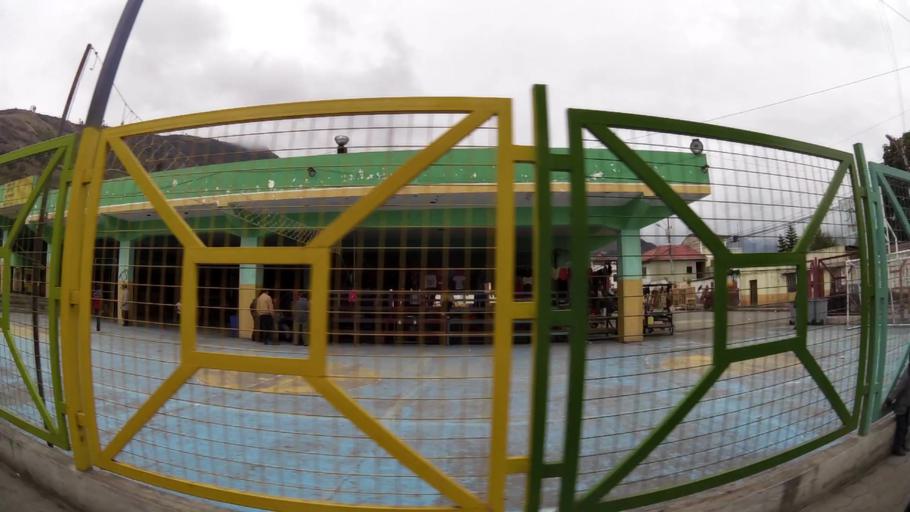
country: EC
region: Chimborazo
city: Alausi
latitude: -2.2908
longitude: -78.9216
